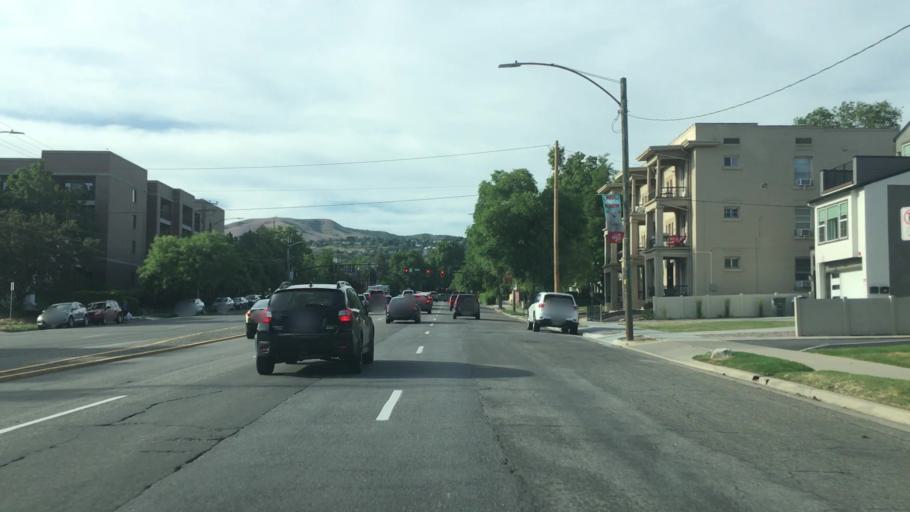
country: US
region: Utah
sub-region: Salt Lake County
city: Salt Lake City
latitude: 40.7657
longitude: -111.8709
